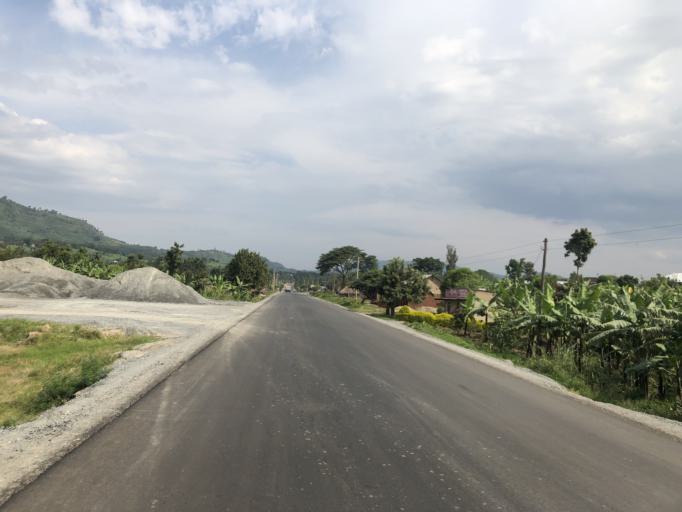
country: UG
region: Western Region
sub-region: Rubirizi District
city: Rubirizi
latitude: -0.2297
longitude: 30.0941
